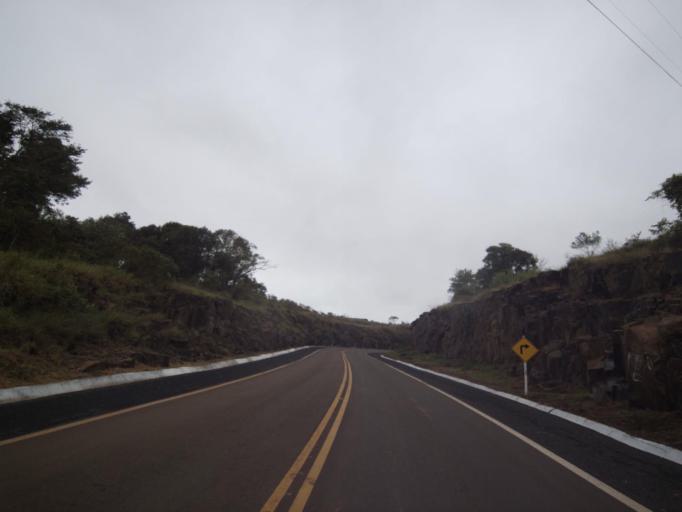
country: AR
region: Misiones
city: El Soberbio
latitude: -27.2890
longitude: -54.1752
